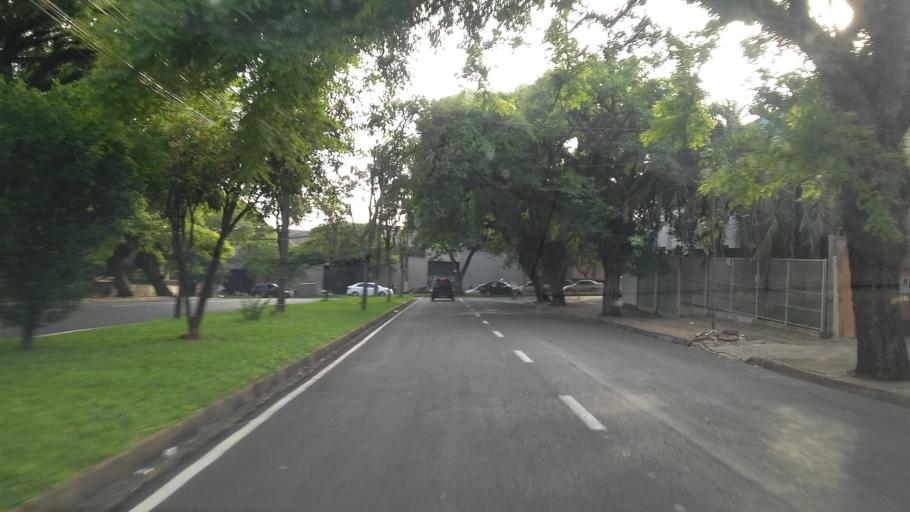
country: BR
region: Parana
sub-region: Londrina
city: Londrina
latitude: -23.3004
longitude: -51.1744
